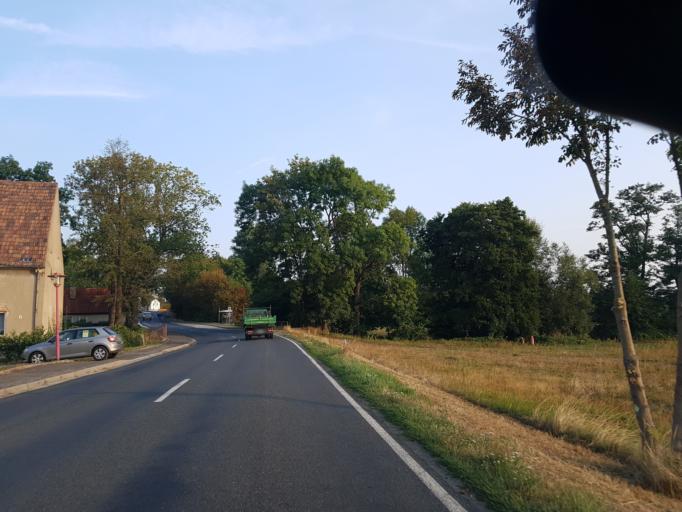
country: DE
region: Saxony
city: Elsnig
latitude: 51.6148
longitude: 12.9120
